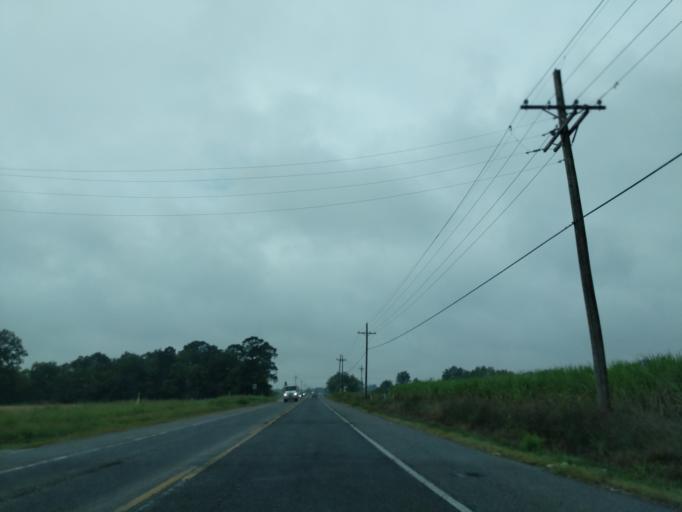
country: US
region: Louisiana
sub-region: Vermilion Parish
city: Abbeville
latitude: 29.9898
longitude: -92.1799
